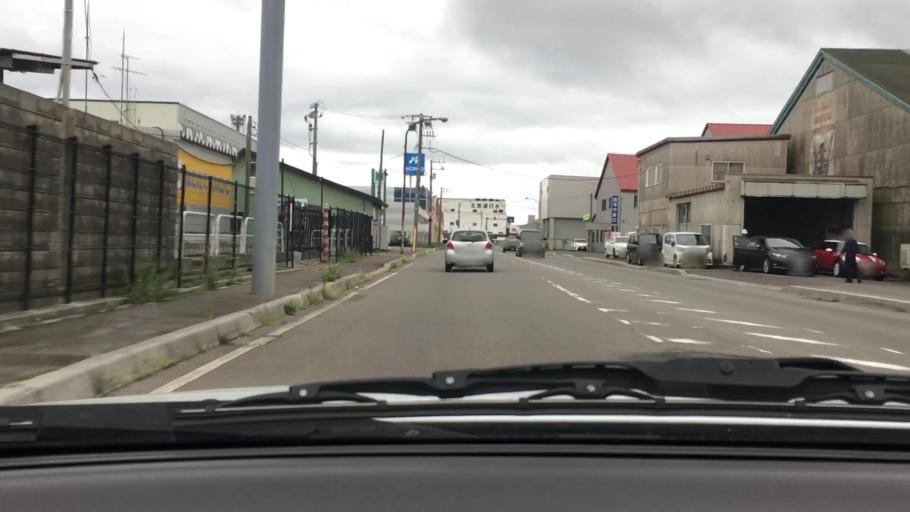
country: JP
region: Hokkaido
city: Hakodate
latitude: 41.7880
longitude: 140.7282
